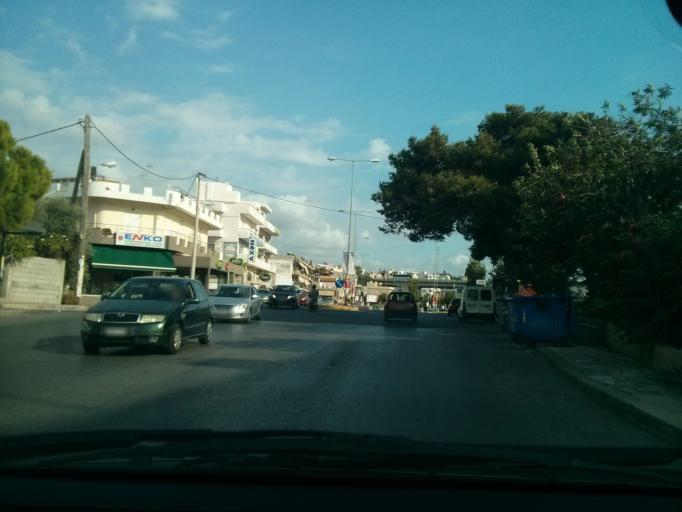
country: GR
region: Crete
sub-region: Nomos Irakleiou
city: Irakleion
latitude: 35.3233
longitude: 25.1411
